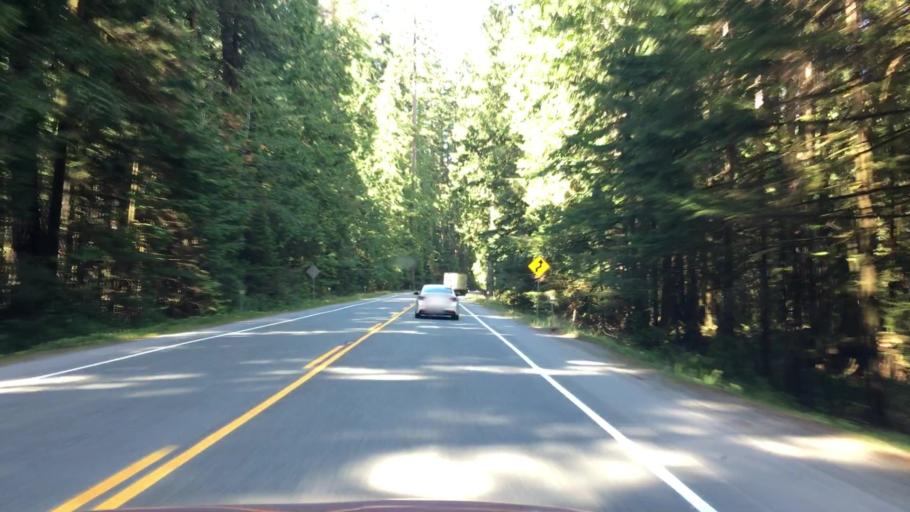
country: CA
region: British Columbia
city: Port Alberni
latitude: 49.2638
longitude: -124.6731
